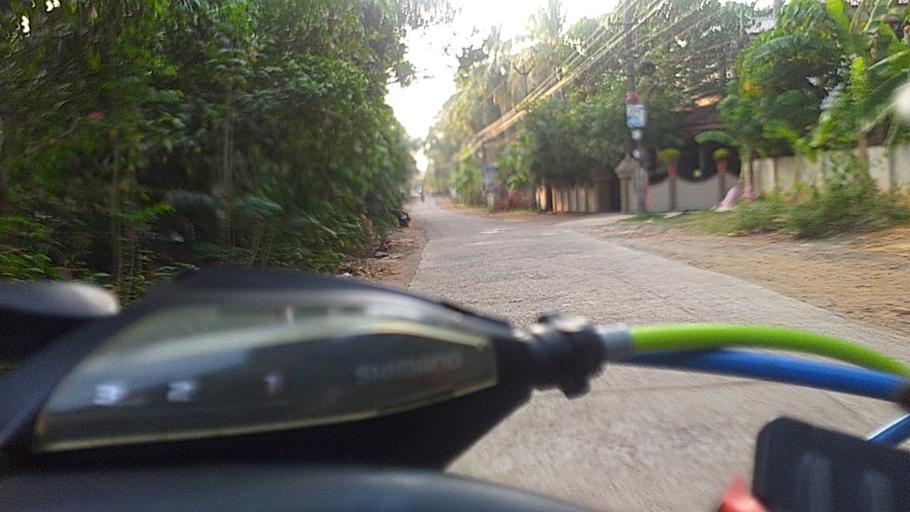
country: IN
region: Kerala
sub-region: Thrissur District
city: Kunnamkulam
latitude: 10.7455
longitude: 76.0338
